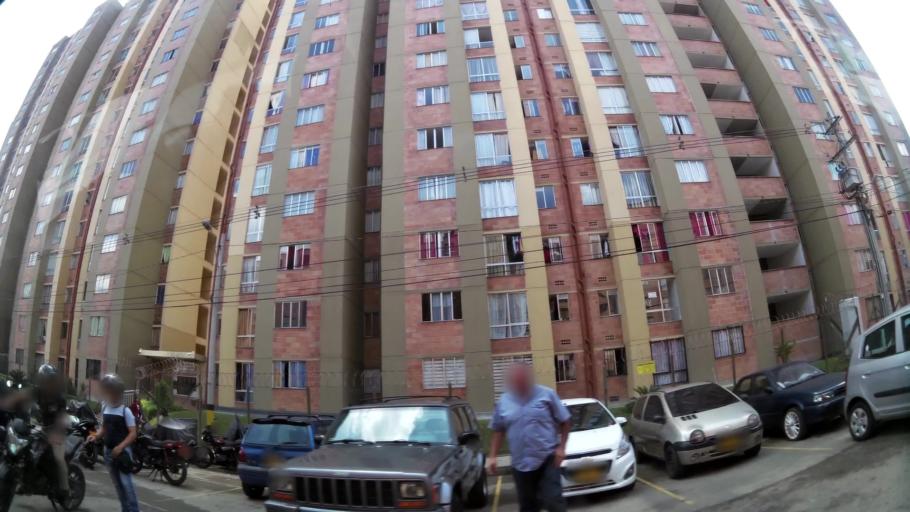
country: CO
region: Antioquia
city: La Estrella
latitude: 6.1749
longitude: -75.6468
